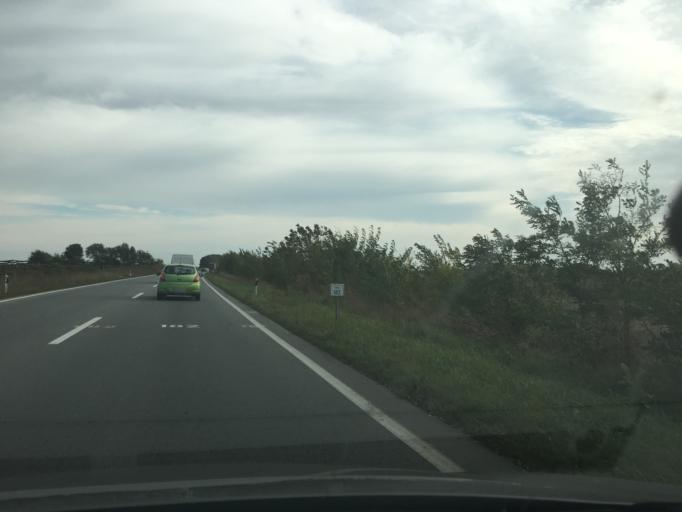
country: RS
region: Autonomna Pokrajina Vojvodina
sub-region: Juznobacki Okrug
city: Petrovaradin
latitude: 45.3176
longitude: 19.9255
